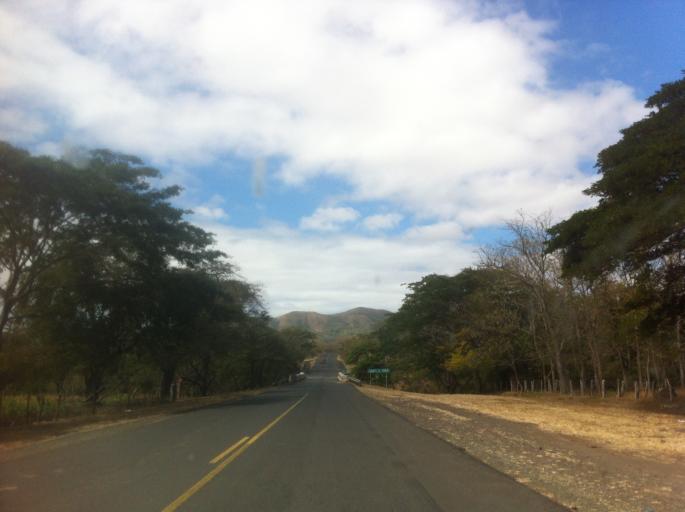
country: NI
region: Chontales
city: Acoyapa
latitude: 12.0032
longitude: -85.1827
